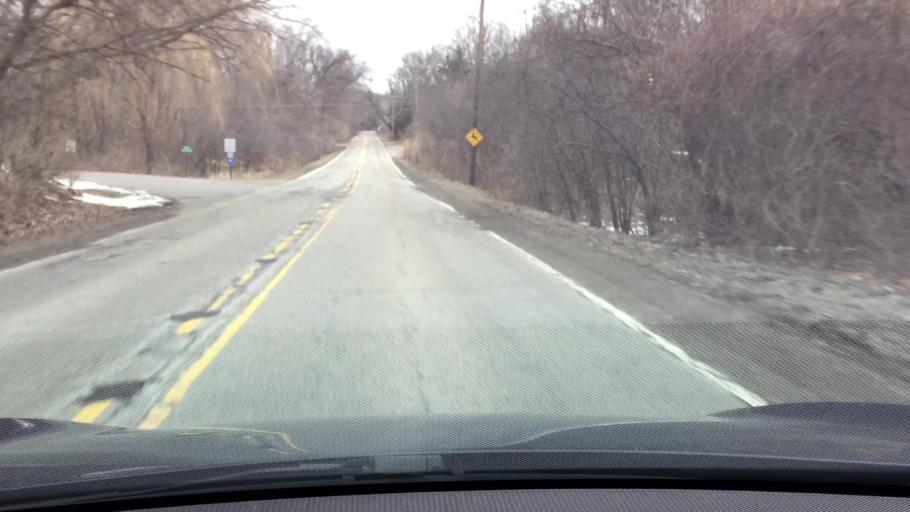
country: US
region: Michigan
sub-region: Oakland County
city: Franklin
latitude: 42.5080
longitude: -83.3100
